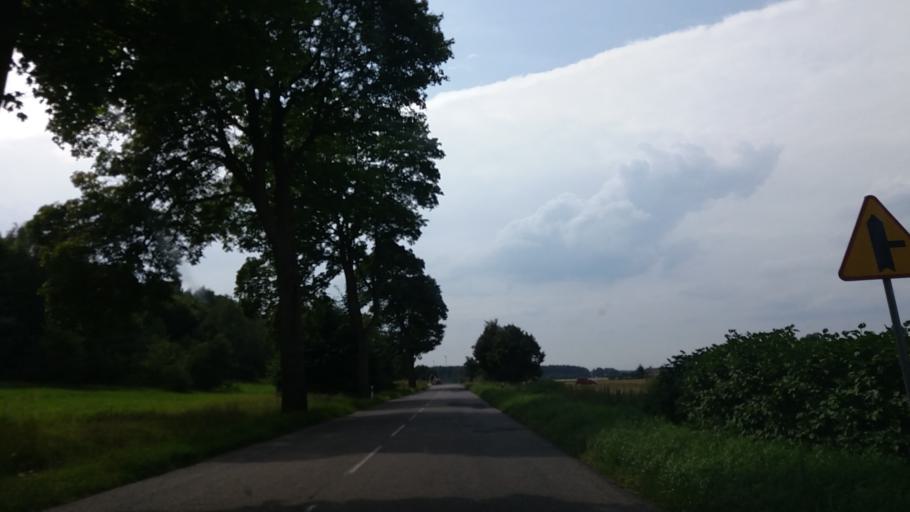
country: PL
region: Lubusz
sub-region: Powiat gorzowski
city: Santok
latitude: 52.7212
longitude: 15.4946
